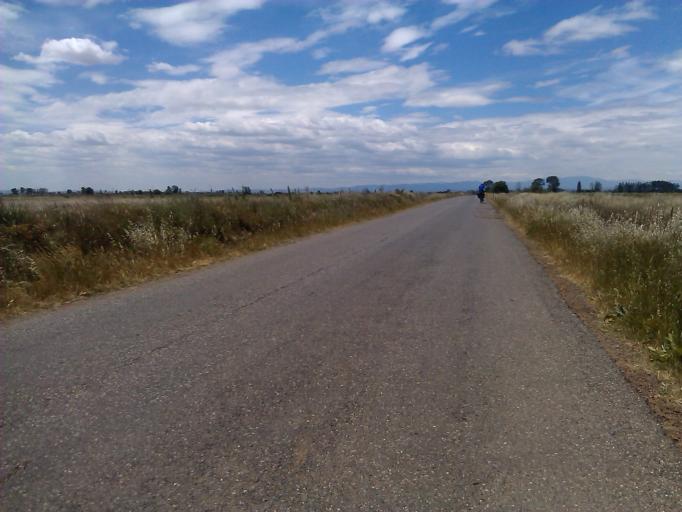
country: ES
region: Castille and Leon
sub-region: Provincia de Leon
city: Villadangos del Paramo
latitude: 42.4749
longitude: -5.7547
